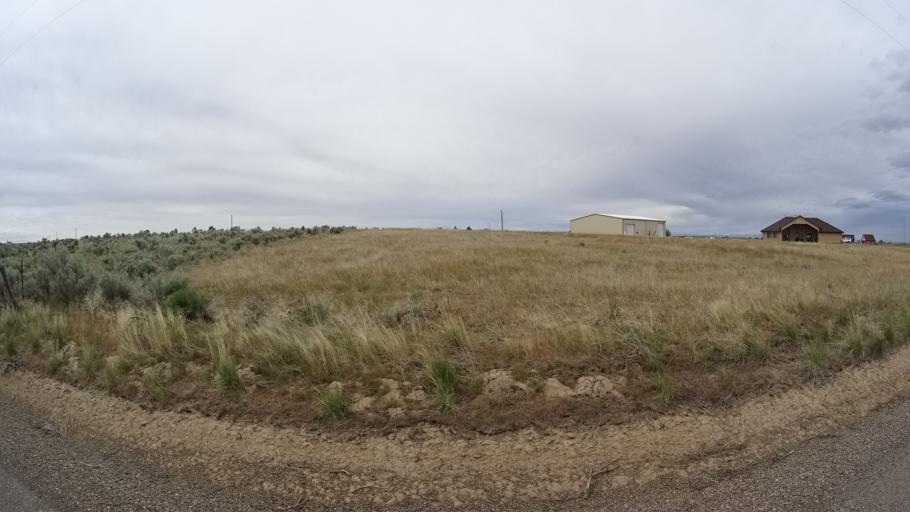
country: US
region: Idaho
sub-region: Ada County
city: Boise
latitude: 43.3869
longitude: -115.9702
